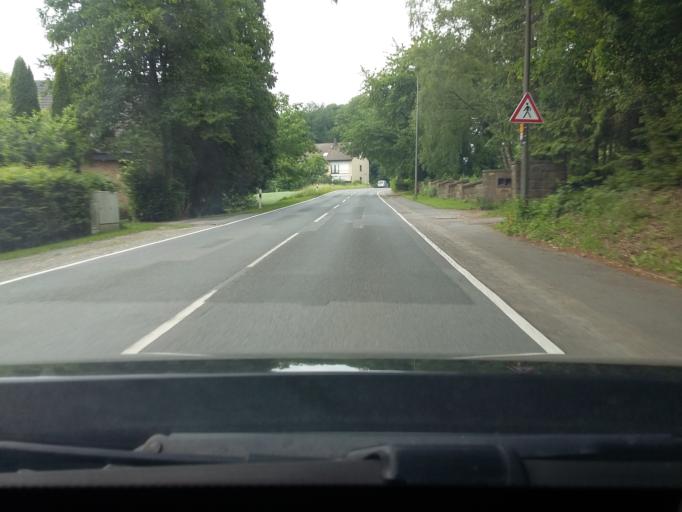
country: DE
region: North Rhine-Westphalia
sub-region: Regierungsbezirk Detmold
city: Bad Salzuflen
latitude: 52.0959
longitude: 8.7660
